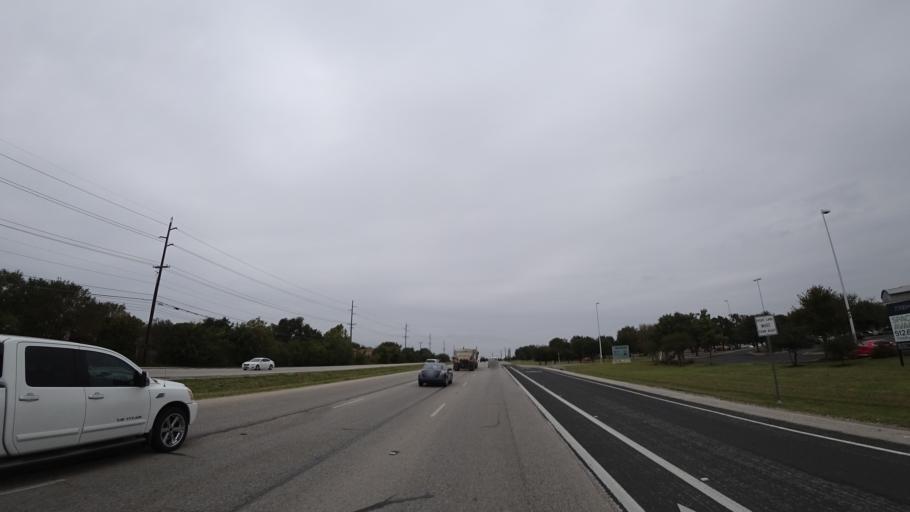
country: US
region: Texas
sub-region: Williamson County
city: Jollyville
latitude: 30.4570
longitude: -97.7530
